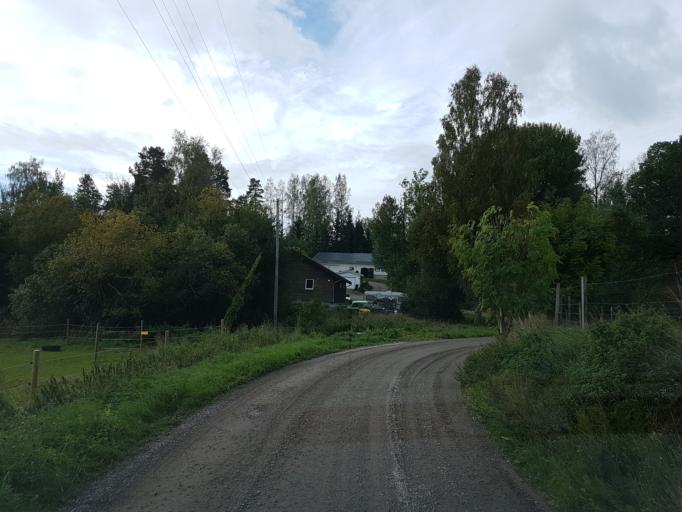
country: SE
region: OEstergoetland
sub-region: Atvidabergs Kommun
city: Atvidaberg
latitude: 58.2175
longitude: 16.0301
